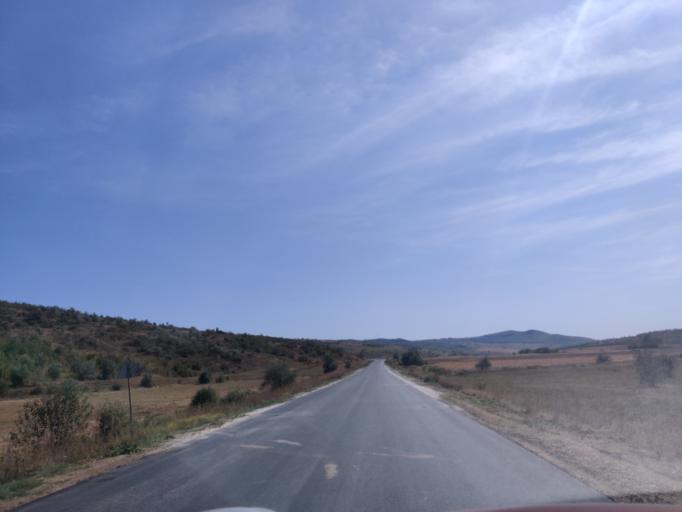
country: MD
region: Ungheni
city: Ungheni
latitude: 47.2508
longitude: 27.9990
